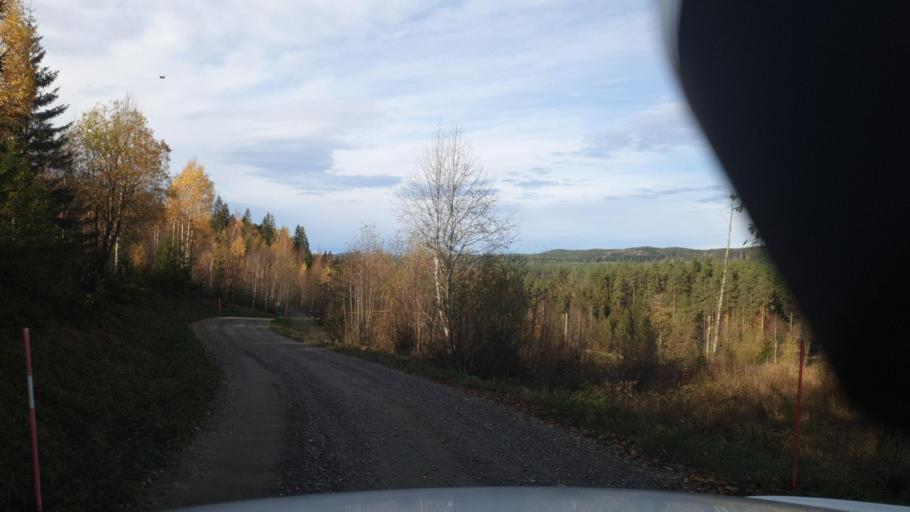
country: SE
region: Vaermland
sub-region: Eda Kommun
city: Charlottenberg
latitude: 60.0676
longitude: 12.5333
